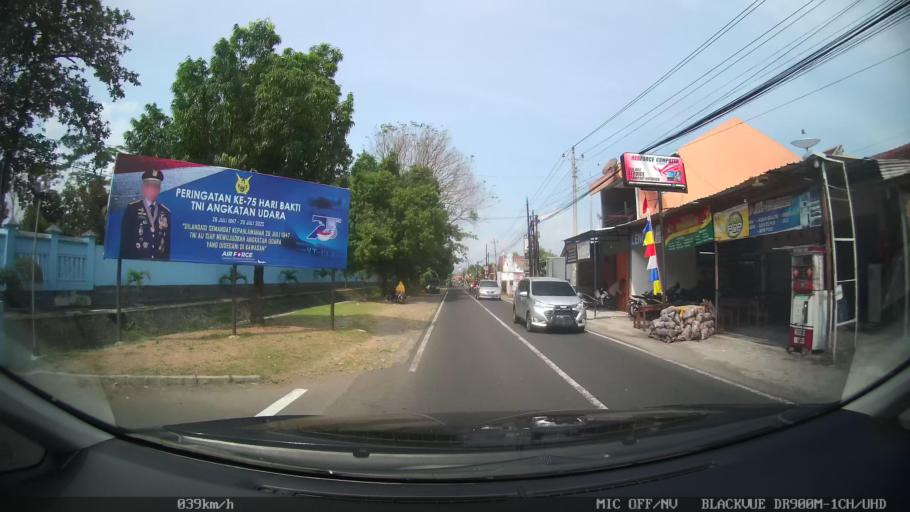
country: ID
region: Daerah Istimewa Yogyakarta
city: Depok
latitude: -7.8039
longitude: 110.4346
